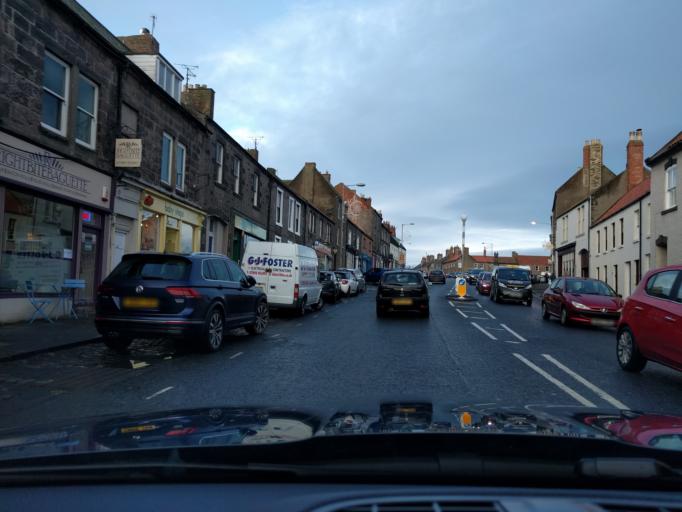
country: GB
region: England
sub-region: Northumberland
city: Berwick-Upon-Tweed
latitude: 55.7722
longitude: -2.0081
